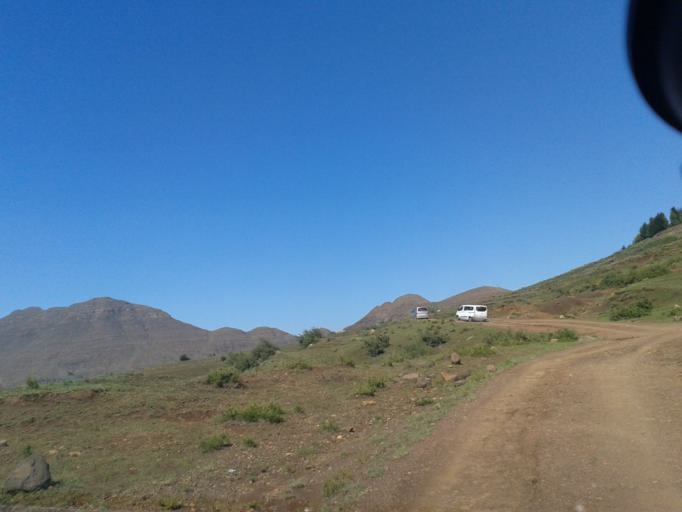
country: LS
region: Maseru
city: Nako
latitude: -29.8419
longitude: 27.5667
